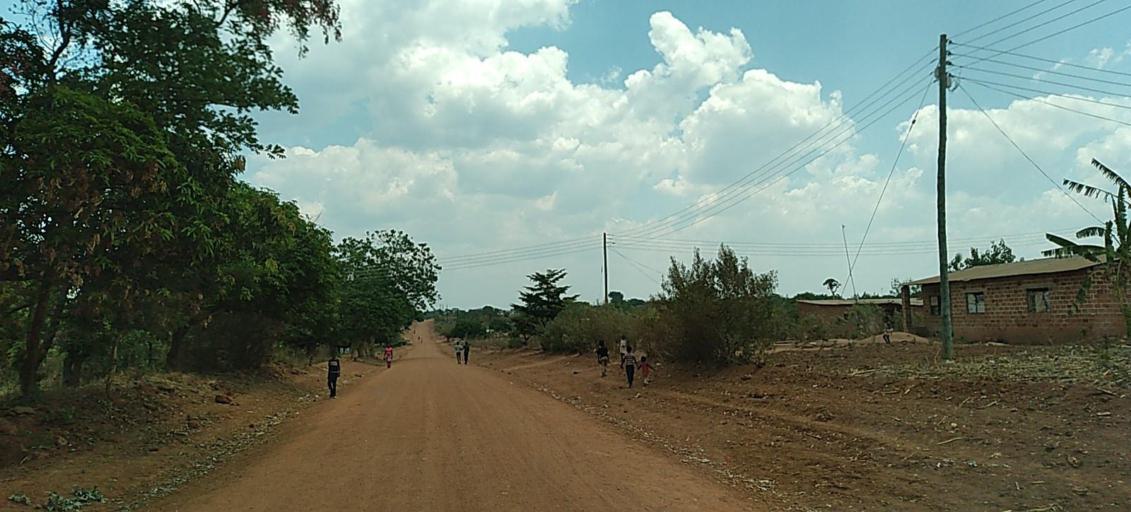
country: ZM
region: Copperbelt
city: Luanshya
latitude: -13.3631
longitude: 28.4126
